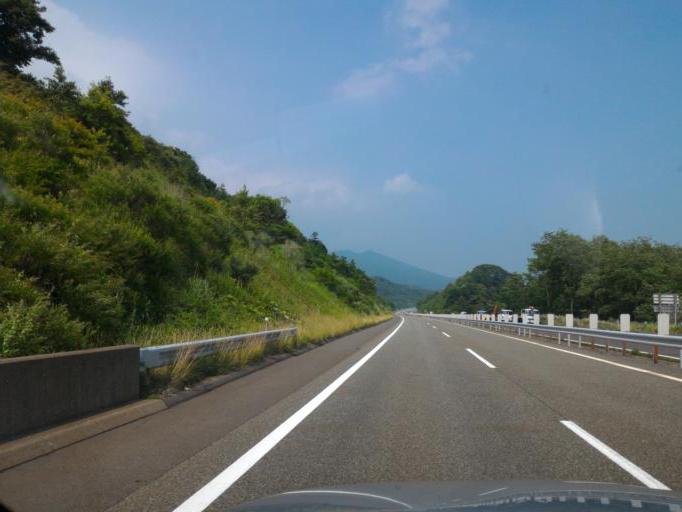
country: JP
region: Hokkaido
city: Shiraoi
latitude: 42.4506
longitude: 141.1597
